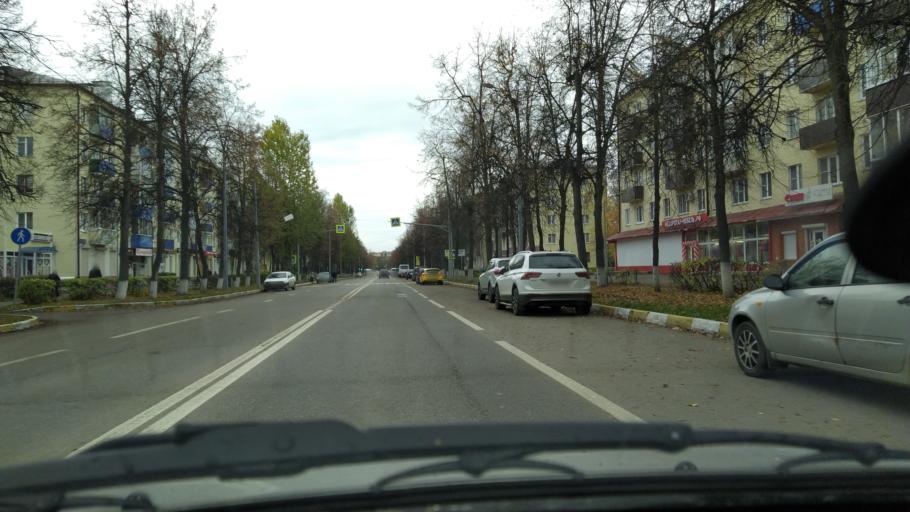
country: RU
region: Moskovskaya
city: Voskresensk
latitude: 55.3252
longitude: 38.6584
